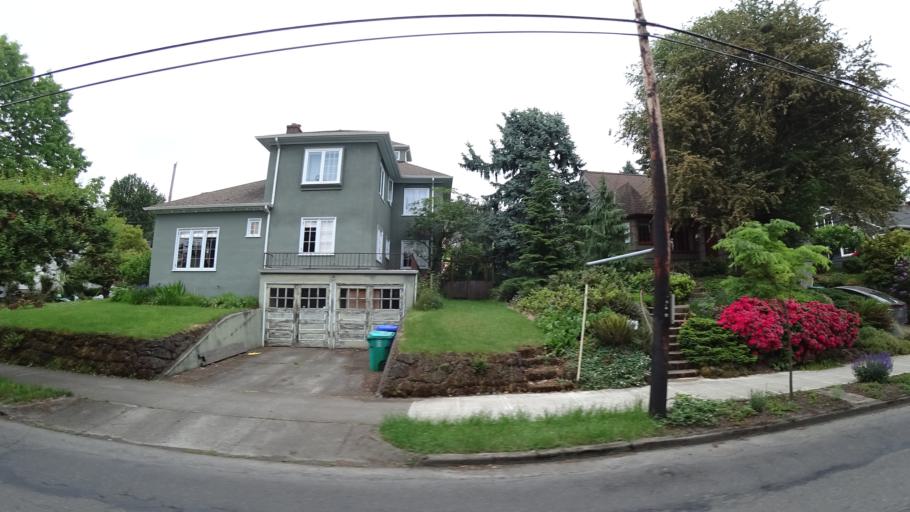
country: US
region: Oregon
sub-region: Multnomah County
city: Lents
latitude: 45.5151
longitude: -122.6020
